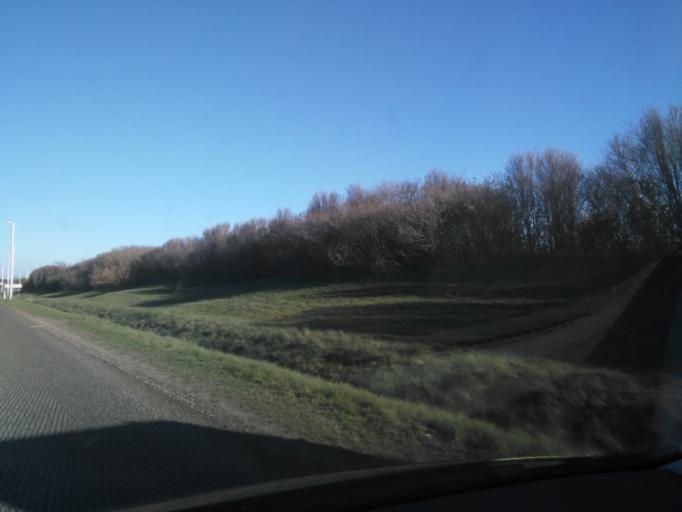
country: DK
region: Central Jutland
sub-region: Ringkobing-Skjern Kommune
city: Videbaek
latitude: 56.0975
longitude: 8.6377
